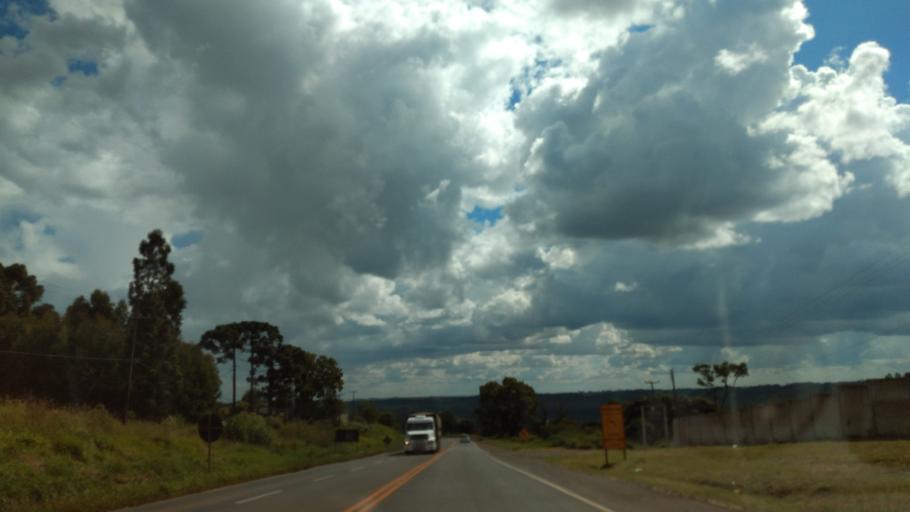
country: BR
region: Parana
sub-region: Guarapuava
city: Guarapuava
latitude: -25.4297
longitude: -51.4948
